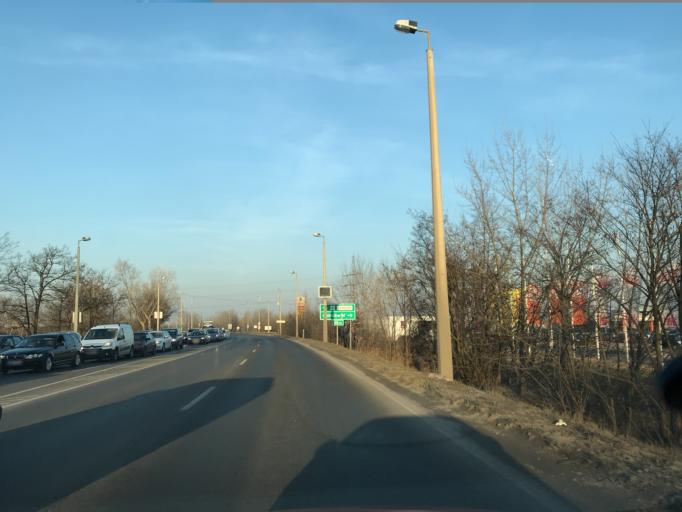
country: HU
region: Gyor-Moson-Sopron
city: Gyor
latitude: 47.6516
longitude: 17.6289
